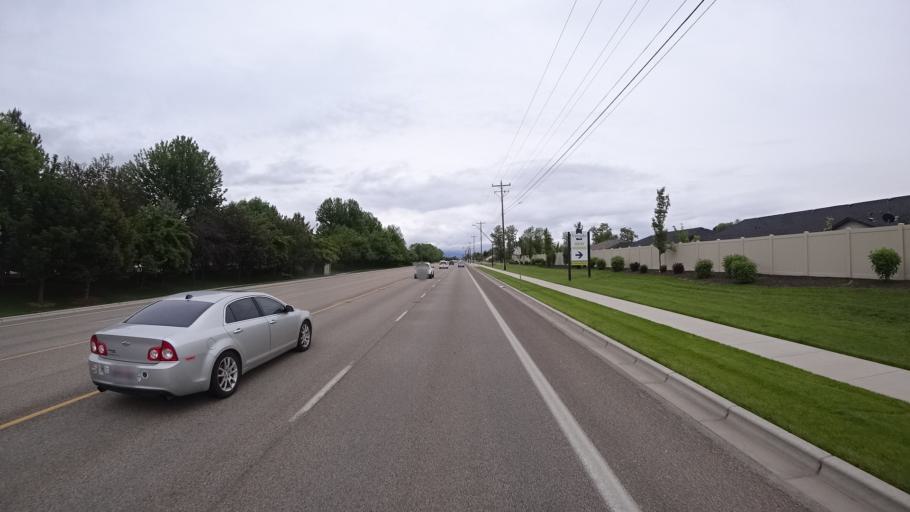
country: US
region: Idaho
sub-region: Ada County
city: Meridian
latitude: 43.6338
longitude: -116.3671
